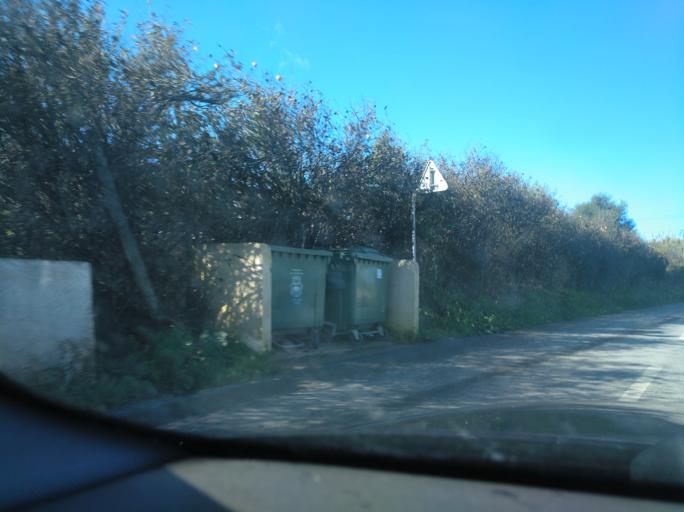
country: PT
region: Faro
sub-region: Vila Real de Santo Antonio
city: Monte Gordo
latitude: 37.1667
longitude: -7.5345
